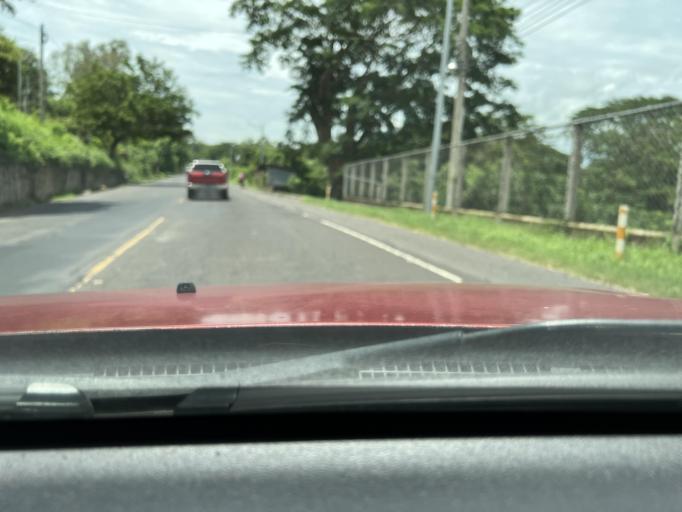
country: SV
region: Usulutan
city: Berlin
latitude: 13.6027
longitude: -88.5857
